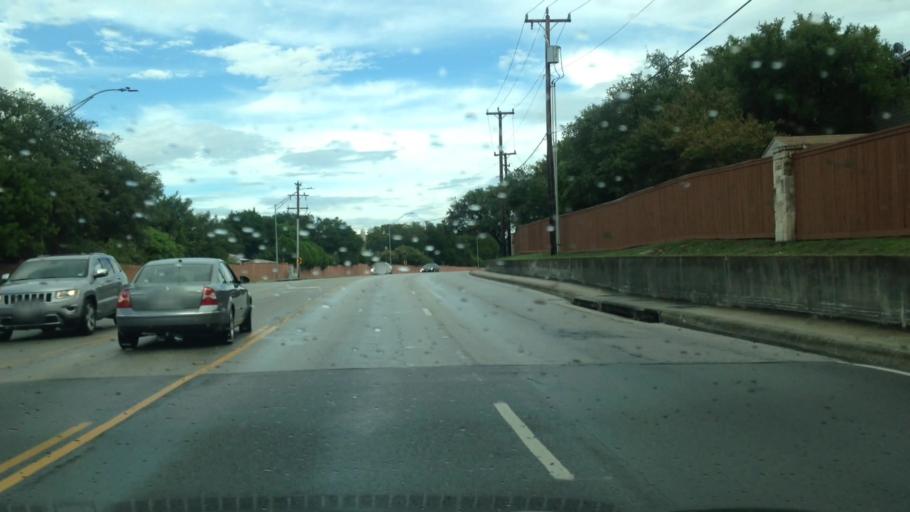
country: US
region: Texas
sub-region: Bexar County
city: Live Oak
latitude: 29.5929
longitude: -98.3995
